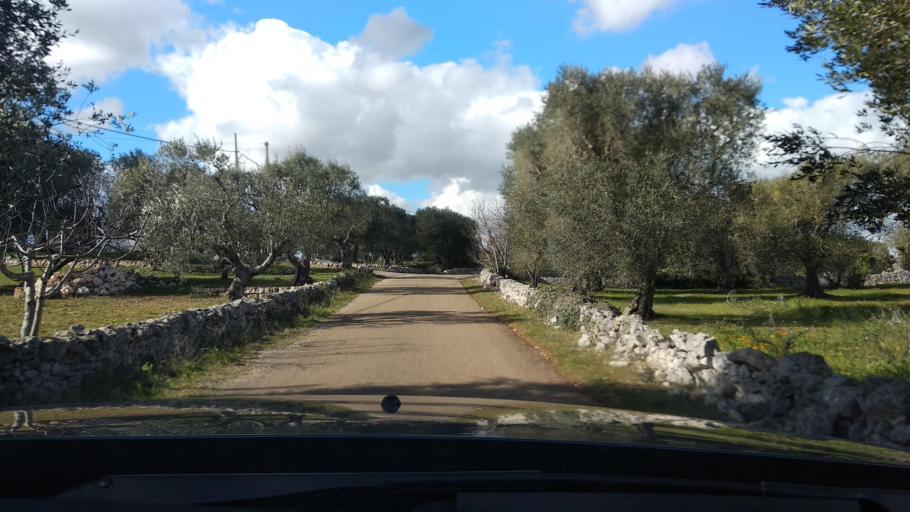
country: IT
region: Apulia
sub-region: Provincia di Brindisi
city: Casalini
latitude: 40.7005
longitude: 17.4634
